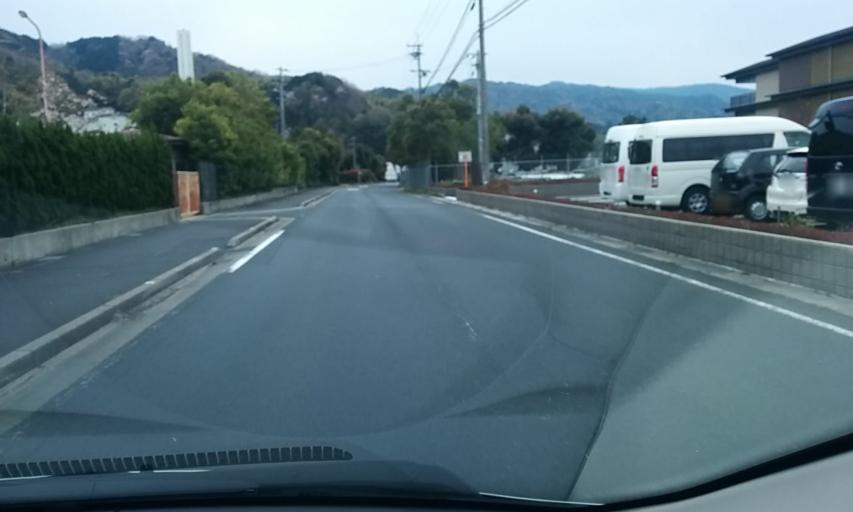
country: JP
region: Kyoto
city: Miyazu
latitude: 35.5508
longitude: 135.2111
